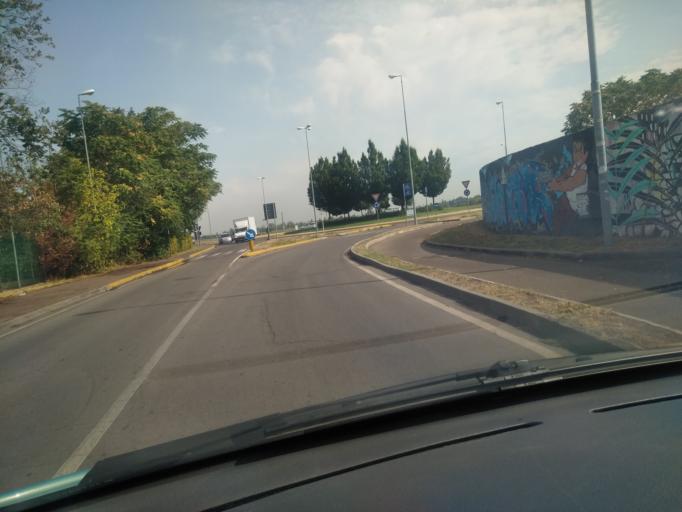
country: IT
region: Emilia-Romagna
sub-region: Provincia di Reggio Emilia
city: Reggio nell'Emilia
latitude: 44.7006
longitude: 10.6526
